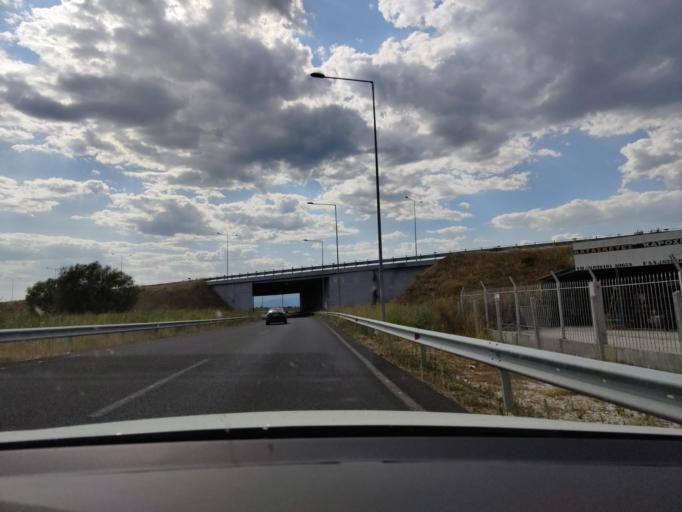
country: GR
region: Central Macedonia
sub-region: Nomos Serron
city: Mitrousi
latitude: 41.0879
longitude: 23.4479
